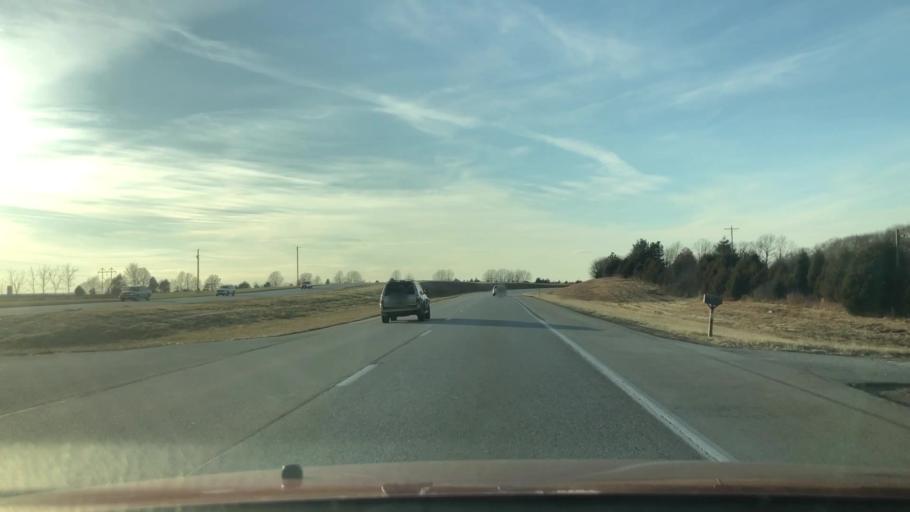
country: US
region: Missouri
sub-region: Webster County
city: Seymour
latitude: 37.1187
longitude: -92.6883
